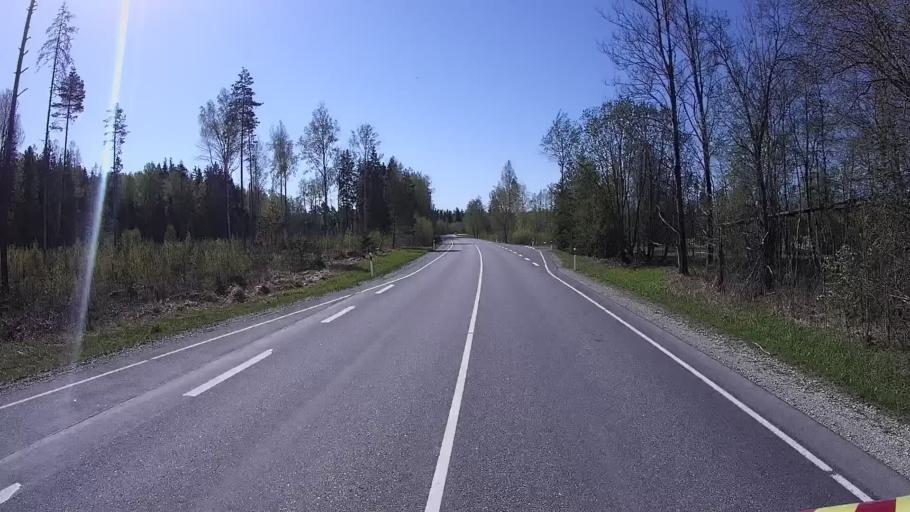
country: EE
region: Raplamaa
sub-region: Jaervakandi vald
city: Jarvakandi
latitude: 58.7570
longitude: 24.8138
